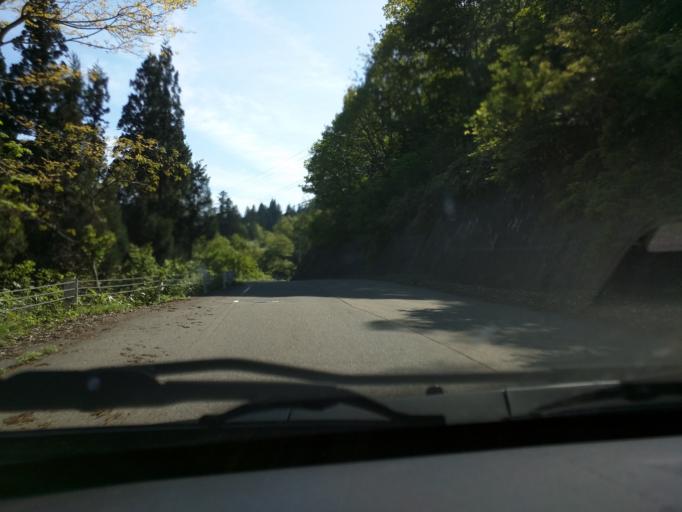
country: JP
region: Fukushima
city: Kitakata
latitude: 37.5624
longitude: 139.6286
